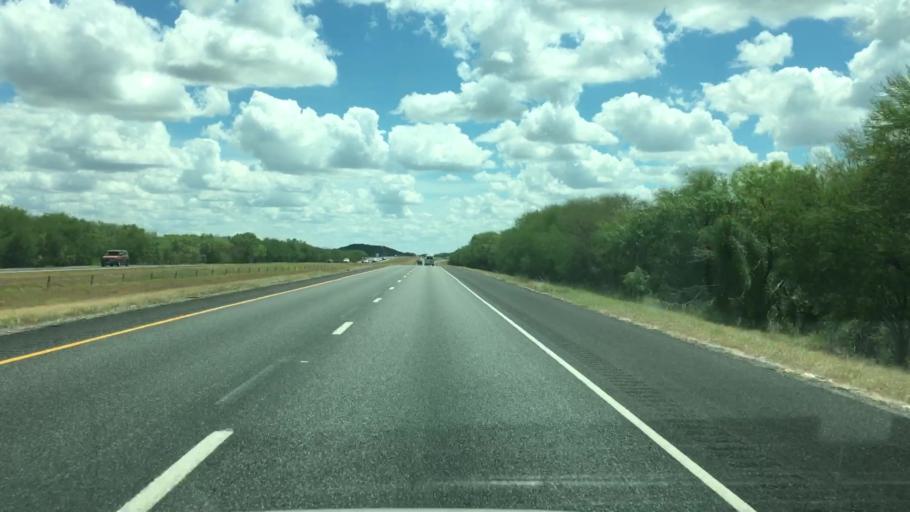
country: US
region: Texas
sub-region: Atascosa County
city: Pleasanton
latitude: 28.7426
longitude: -98.2925
